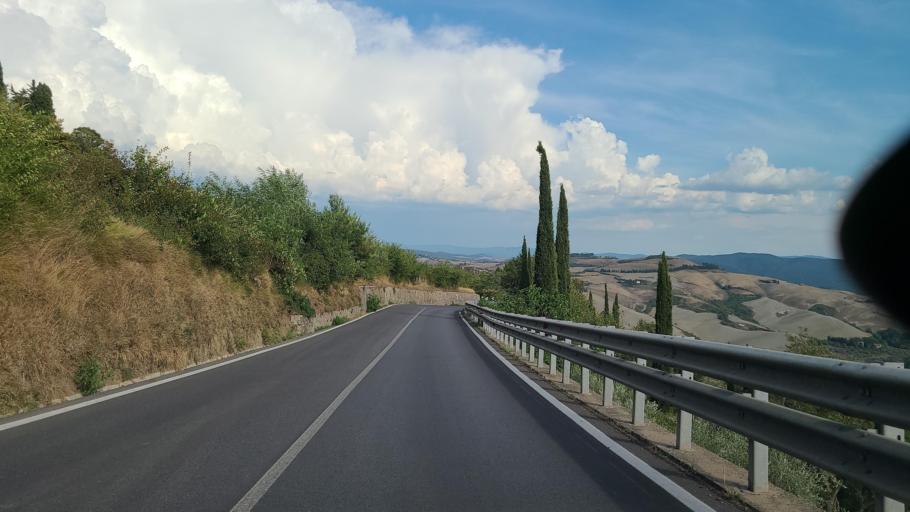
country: IT
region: Tuscany
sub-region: Province of Pisa
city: Volterra
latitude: 43.3971
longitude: 10.8773
